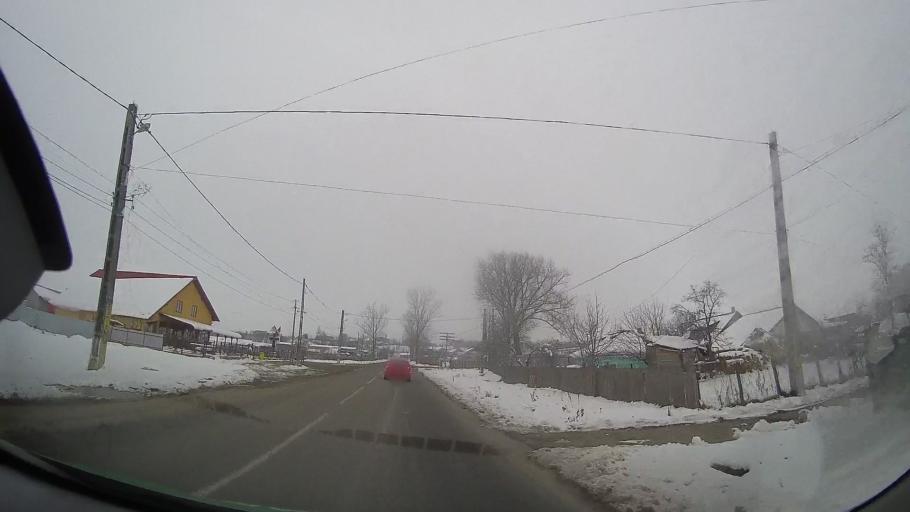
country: RO
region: Vaslui
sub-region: Comuna Negresti
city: Negresti
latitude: 46.8388
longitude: 27.3997
